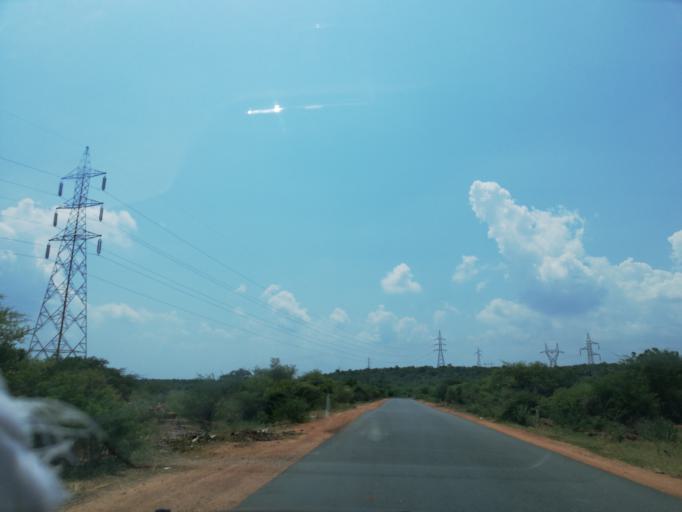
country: IN
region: Andhra Pradesh
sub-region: Guntur
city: Macherla
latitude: 16.5665
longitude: 79.3477
